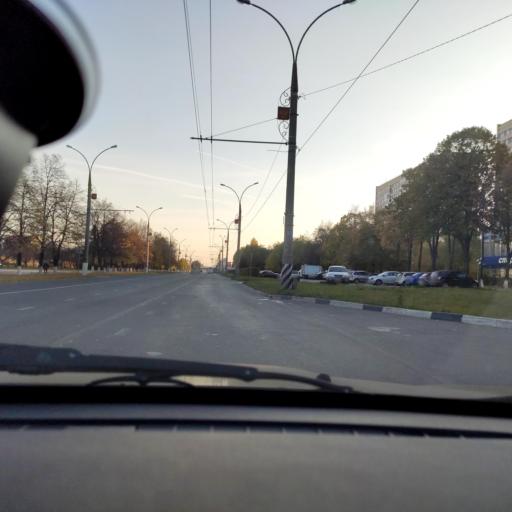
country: RU
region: Samara
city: Tol'yatti
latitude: 53.5240
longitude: 49.2749
